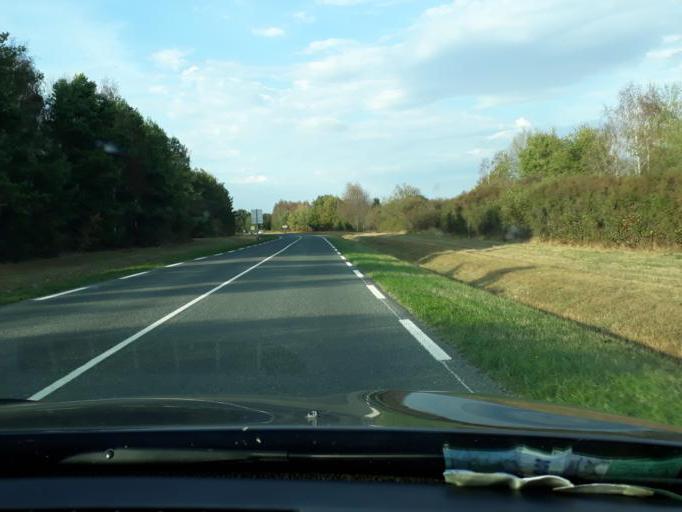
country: FR
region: Centre
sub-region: Departement du Loiret
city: Chateauneuf-sur-Loire
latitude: 47.8760
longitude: 2.2378
